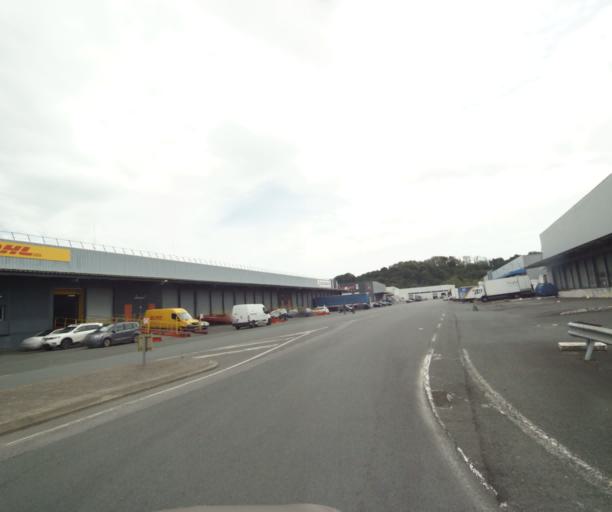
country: FR
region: Aquitaine
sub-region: Departement des Pyrenees-Atlantiques
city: Mouguerre
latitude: 43.4879
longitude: -1.4280
